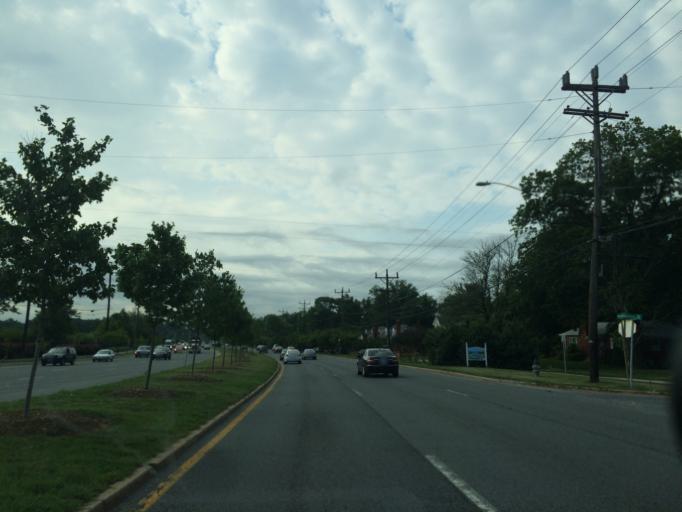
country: US
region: Maryland
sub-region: Montgomery County
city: White Oak
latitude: 39.0363
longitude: -76.9890
